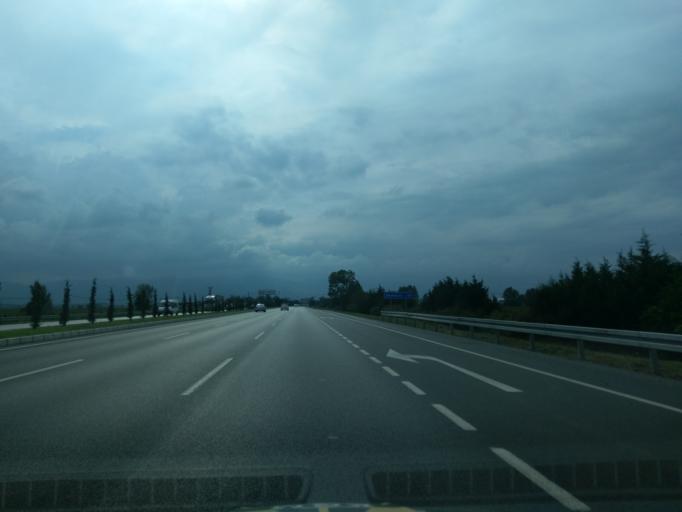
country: TR
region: Samsun
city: Tekkekoy
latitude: 41.2362
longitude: 36.5325
